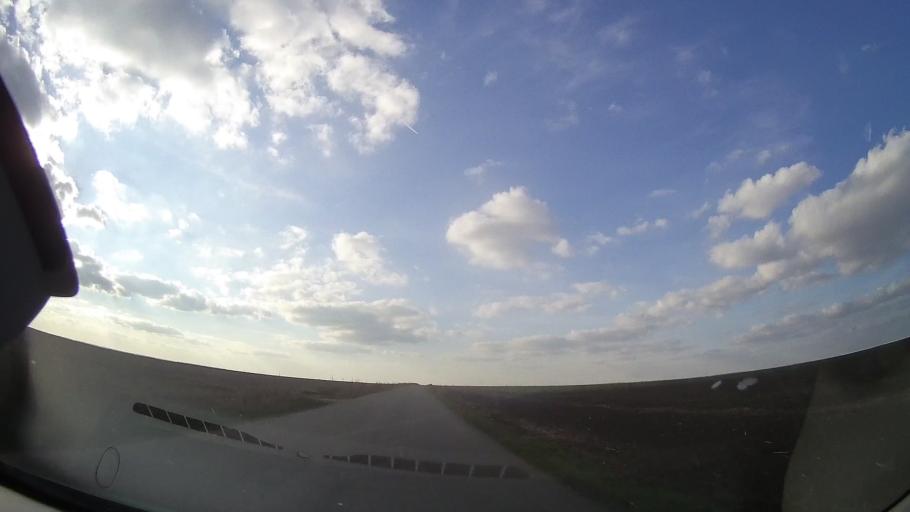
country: RO
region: Constanta
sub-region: Comuna Cerchezu
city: Cerchezu
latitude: 43.8235
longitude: 28.1464
